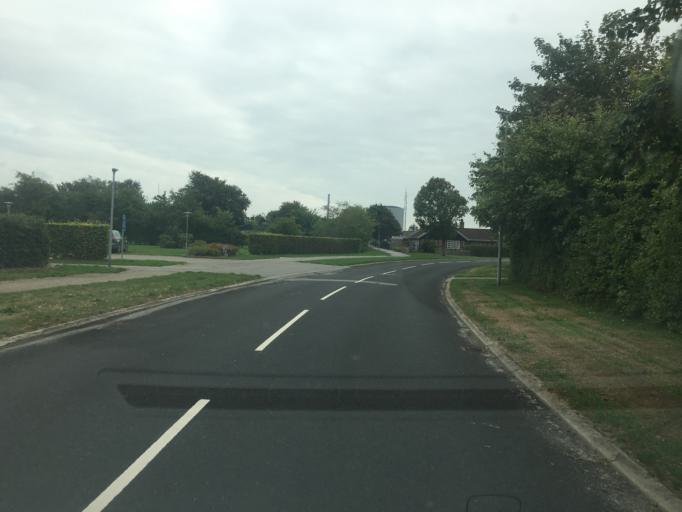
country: DK
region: South Denmark
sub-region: Tonder Kommune
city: Tonder
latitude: 54.9330
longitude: 8.8521
